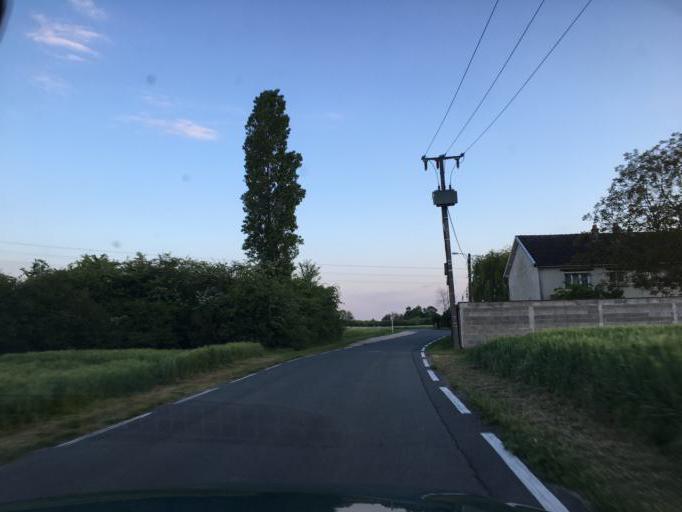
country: FR
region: Centre
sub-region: Departement du Loiret
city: Saint-Jean-de-la-Ruelle
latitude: 47.9303
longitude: 1.8710
